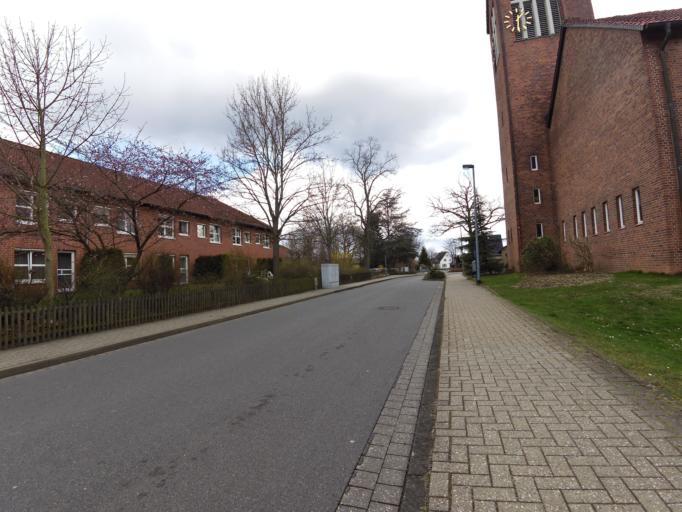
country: DE
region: Lower Saxony
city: Hambuhren
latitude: 52.6034
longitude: 10.0195
